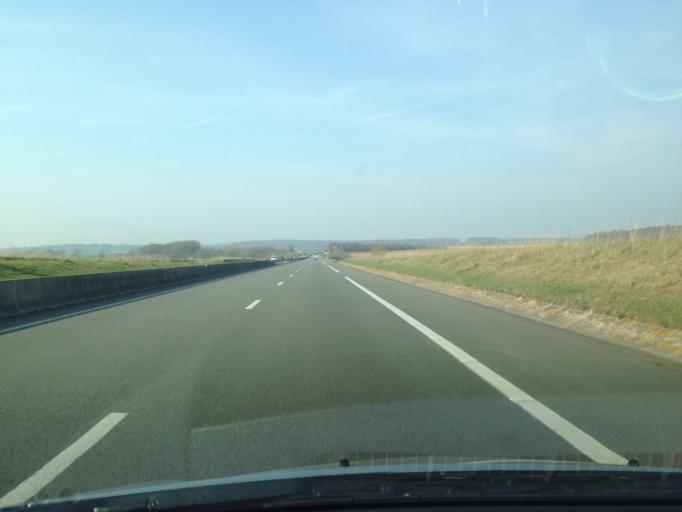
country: FR
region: Nord-Pas-de-Calais
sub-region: Departement du Pas-de-Calais
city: Saint-Josse
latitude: 50.4313
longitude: 1.6940
